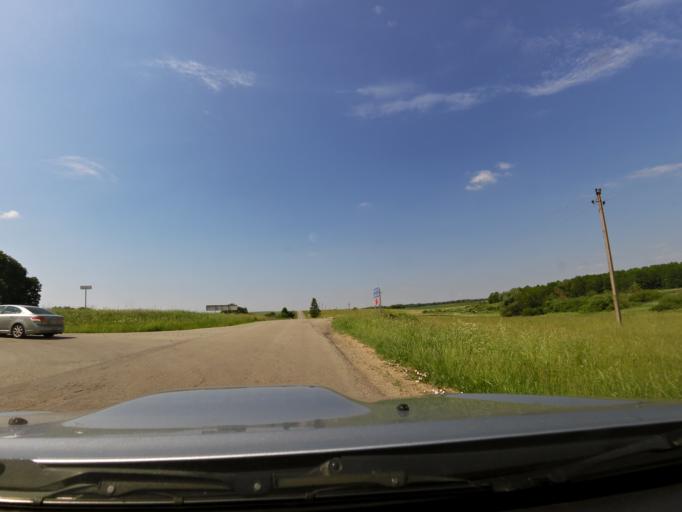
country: LT
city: Vilkaviskis
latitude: 54.5076
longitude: 22.9958
